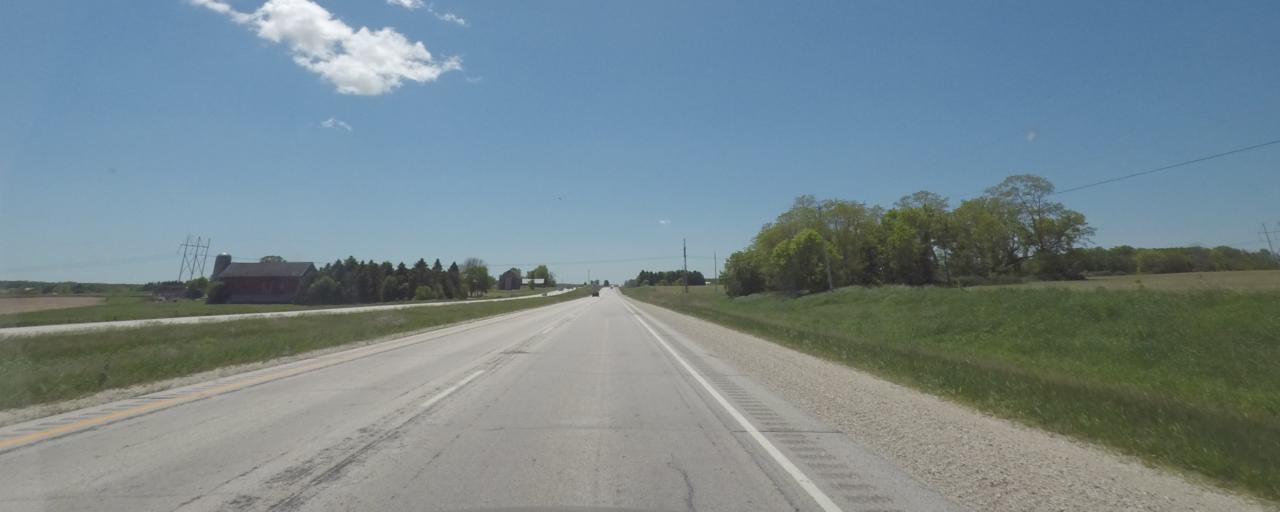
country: US
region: Wisconsin
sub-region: Sheboygan County
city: Plymouth
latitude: 43.7133
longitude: -87.9409
